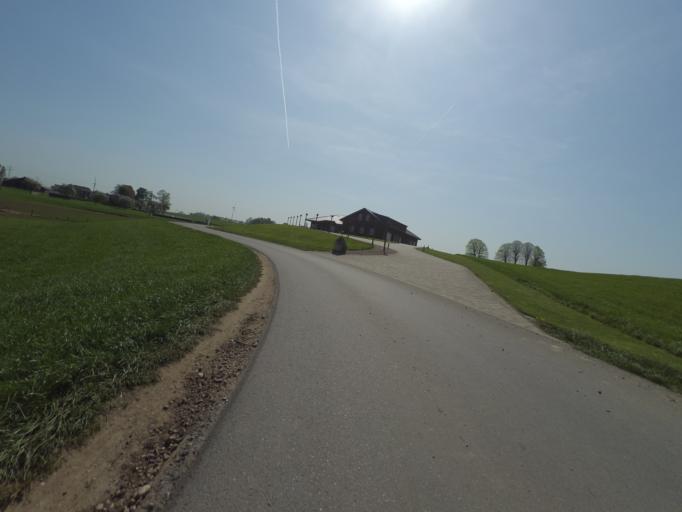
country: DE
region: North Rhine-Westphalia
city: Rees
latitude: 51.7187
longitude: 6.4379
